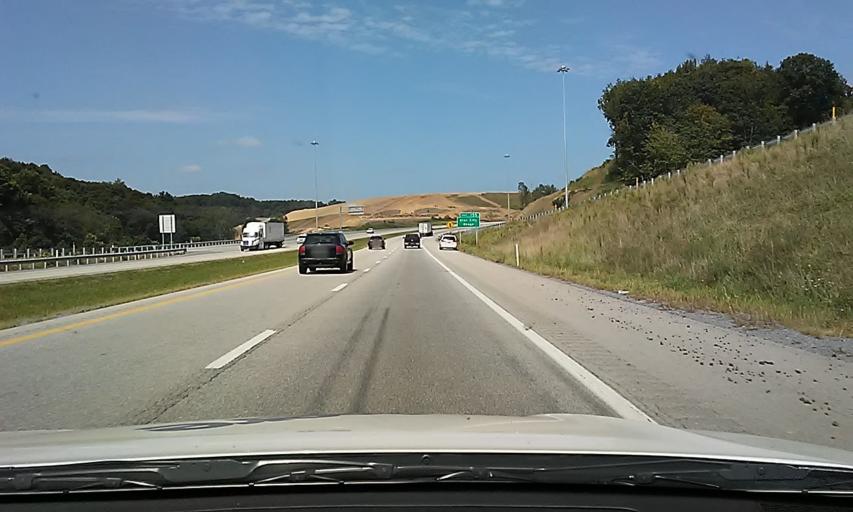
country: US
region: West Virginia
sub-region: Monongalia County
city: Star City
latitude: 39.6412
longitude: -80.0034
